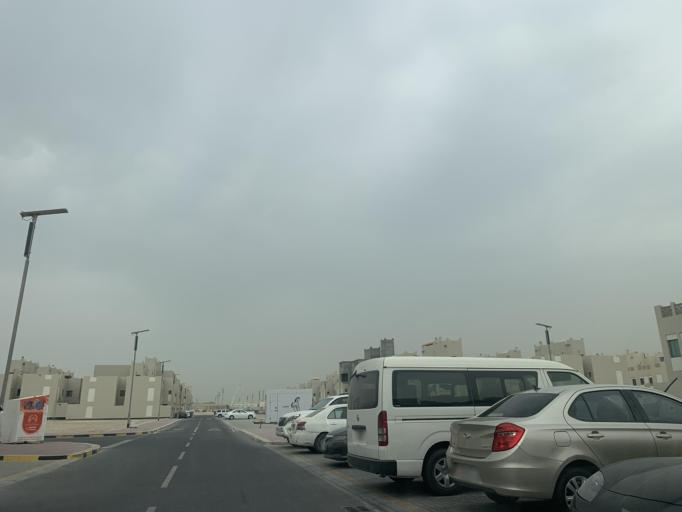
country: BH
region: Northern
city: Madinat `Isa
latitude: 26.1691
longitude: 50.5103
